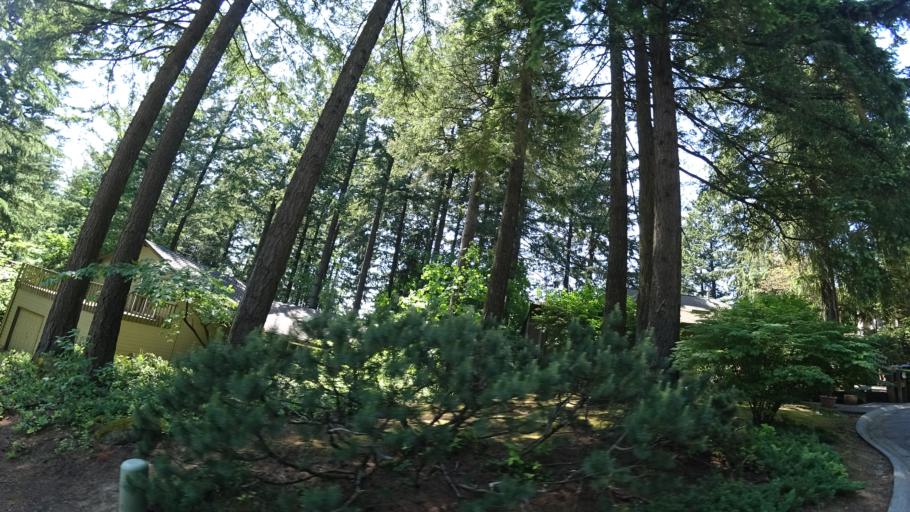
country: US
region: Oregon
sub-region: Washington County
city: Metzger
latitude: 45.4329
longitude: -122.7225
